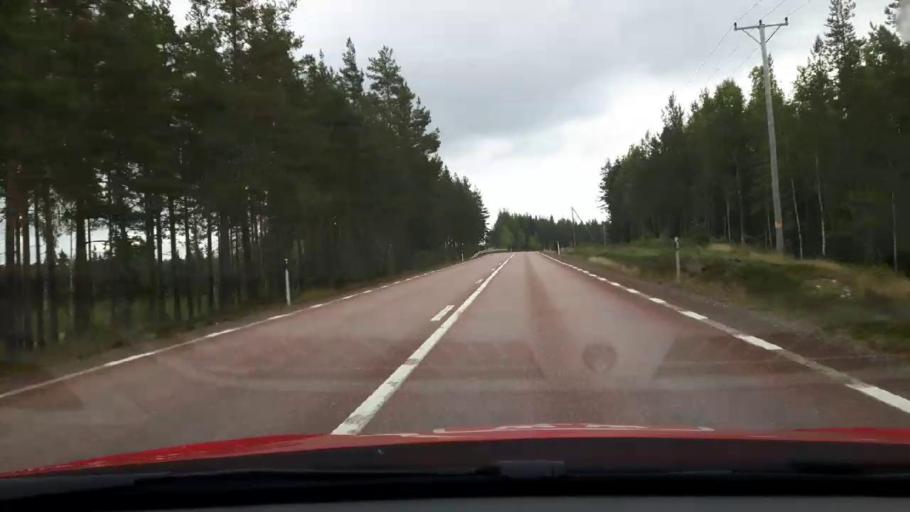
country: SE
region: Gaevleborg
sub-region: Soderhamns Kommun
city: Soderhamn
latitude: 61.1254
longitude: 16.9316
